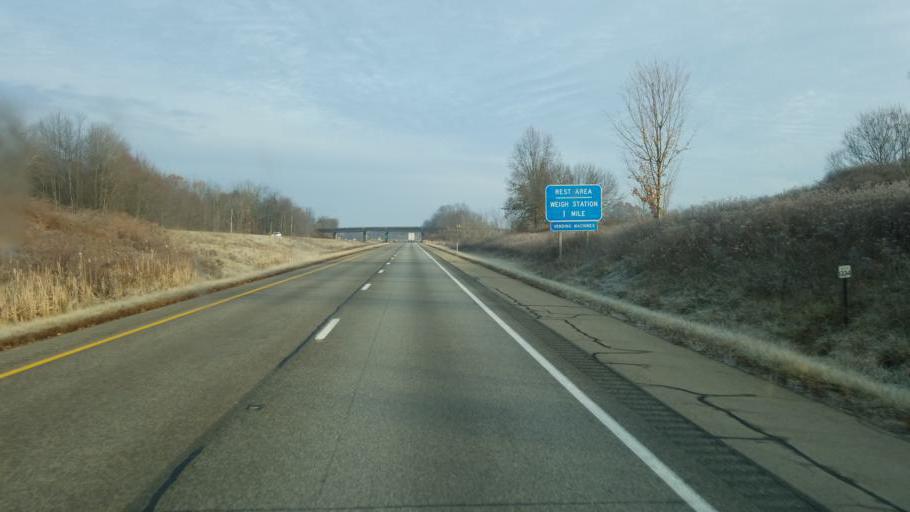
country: US
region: Pennsylvania
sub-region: Mercer County
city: Stoneboro
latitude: 41.4394
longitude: -80.1616
